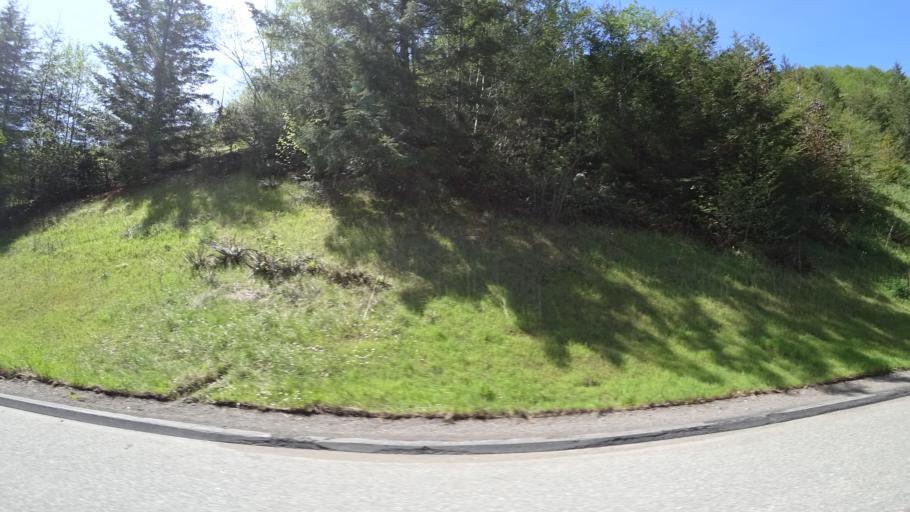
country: US
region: California
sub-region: Del Norte County
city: Bertsch-Oceanview
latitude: 41.4239
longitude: -124.0003
